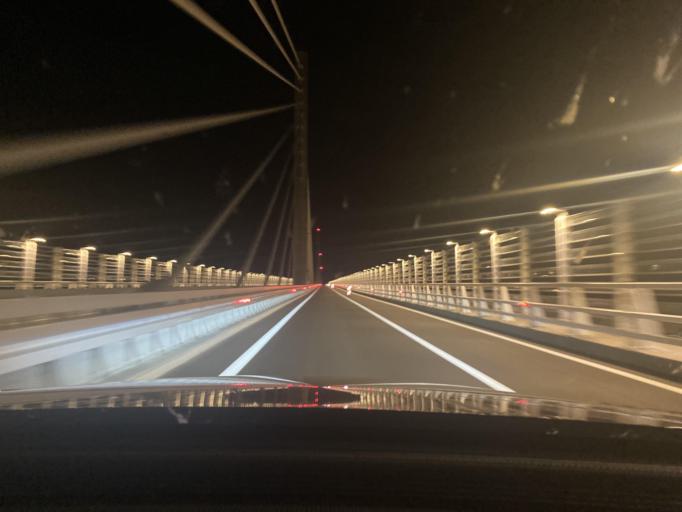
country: BA
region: Federation of Bosnia and Herzegovina
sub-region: Hercegovacko-Bosanski Kanton
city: Neum
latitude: 42.9377
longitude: 17.5417
